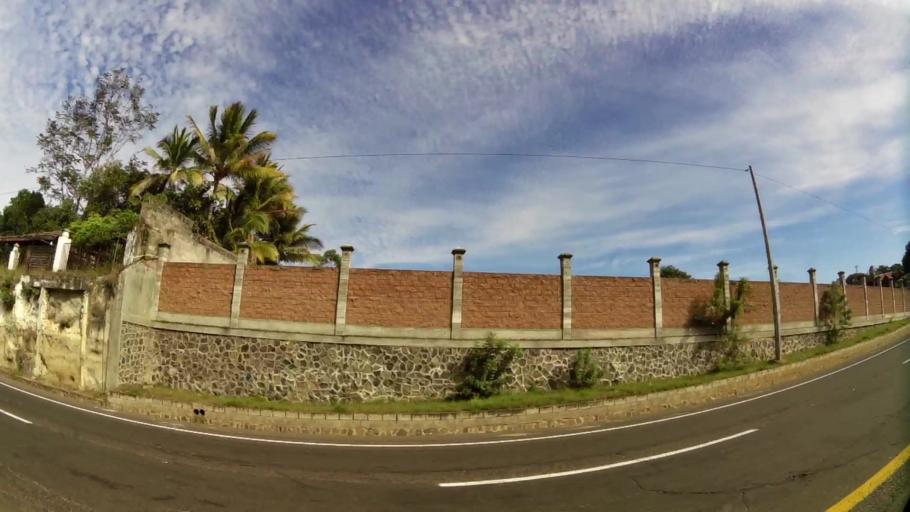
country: SV
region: Santa Ana
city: Chalchuapa
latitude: 13.9854
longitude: -89.6909
